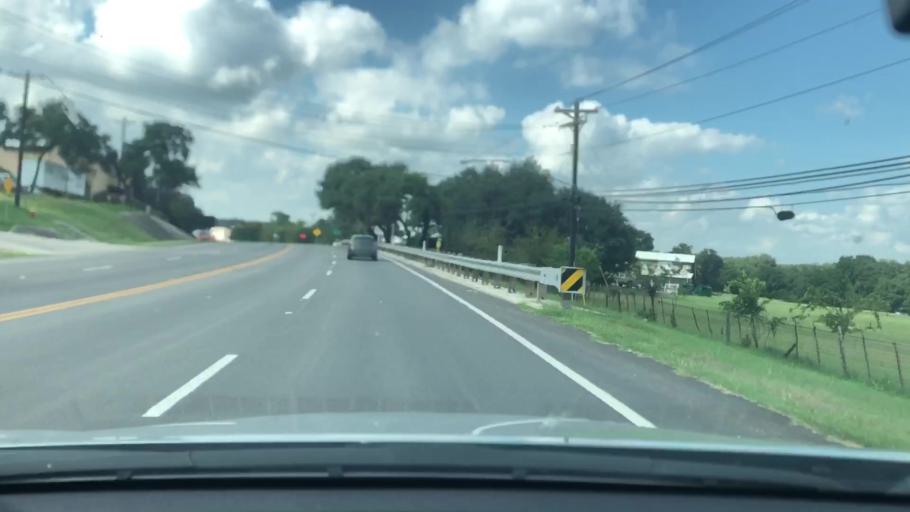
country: US
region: Texas
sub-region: Kendall County
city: Boerne
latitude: 29.7729
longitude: -98.7209
